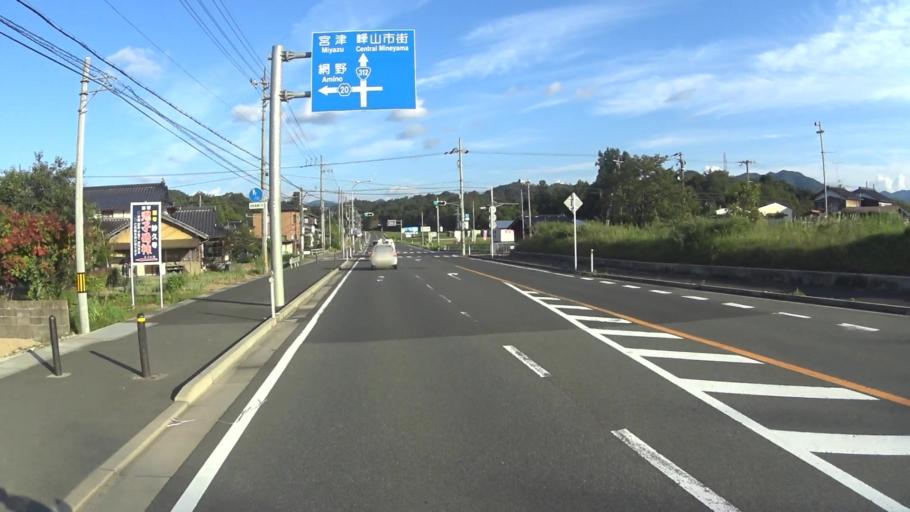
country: JP
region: Hyogo
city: Toyooka
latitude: 35.5898
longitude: 134.9416
